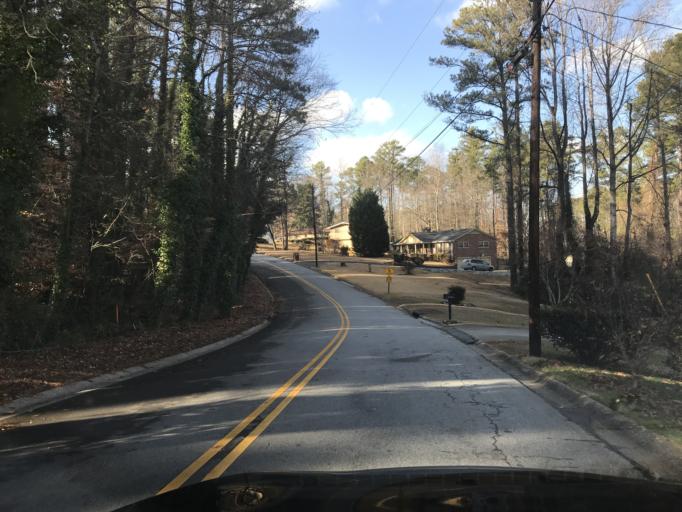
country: US
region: Georgia
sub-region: Fulton County
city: College Park
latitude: 33.6437
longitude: -84.4759
